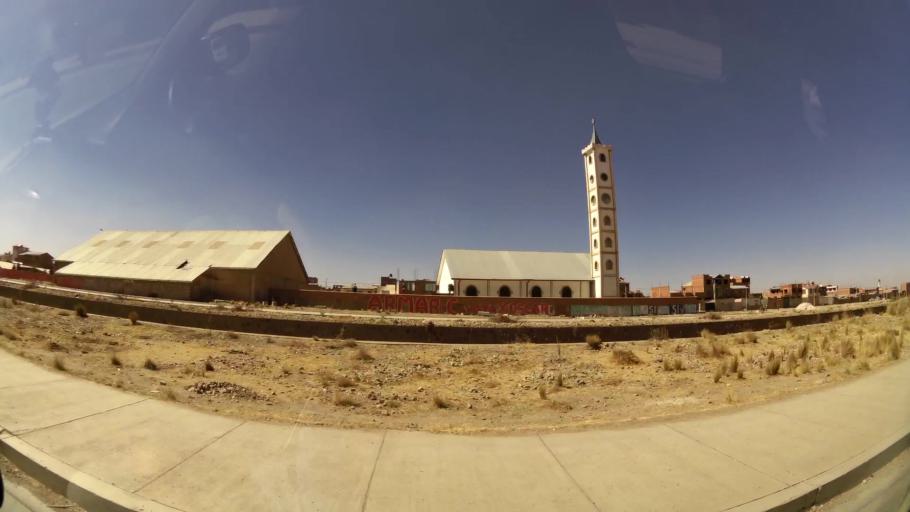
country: BO
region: La Paz
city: La Paz
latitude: -16.5068
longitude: -68.2118
